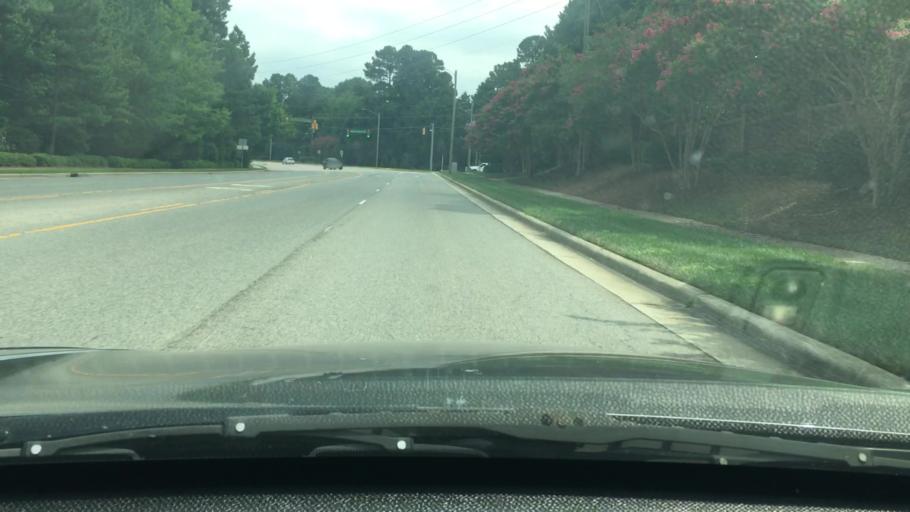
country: US
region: North Carolina
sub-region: Wake County
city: West Raleigh
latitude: 35.8281
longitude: -78.7107
